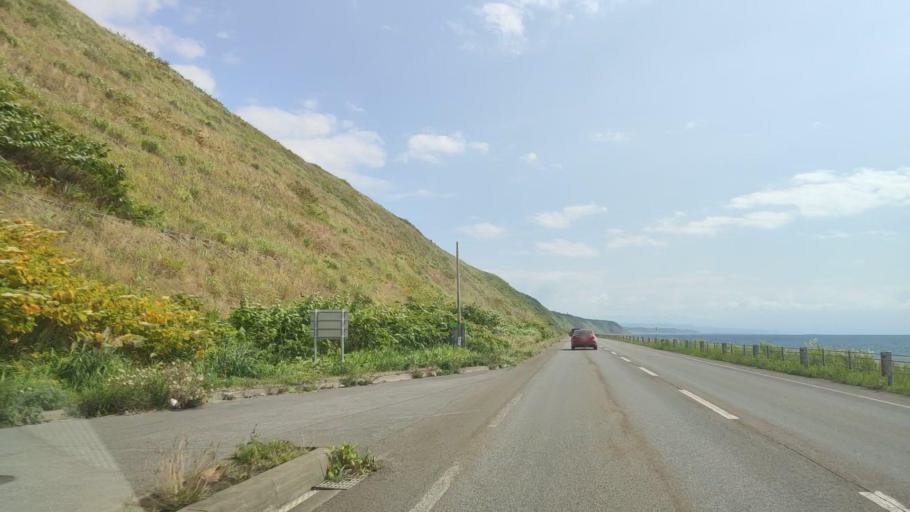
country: JP
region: Hokkaido
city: Rumoi
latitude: 44.0674
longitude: 141.6629
